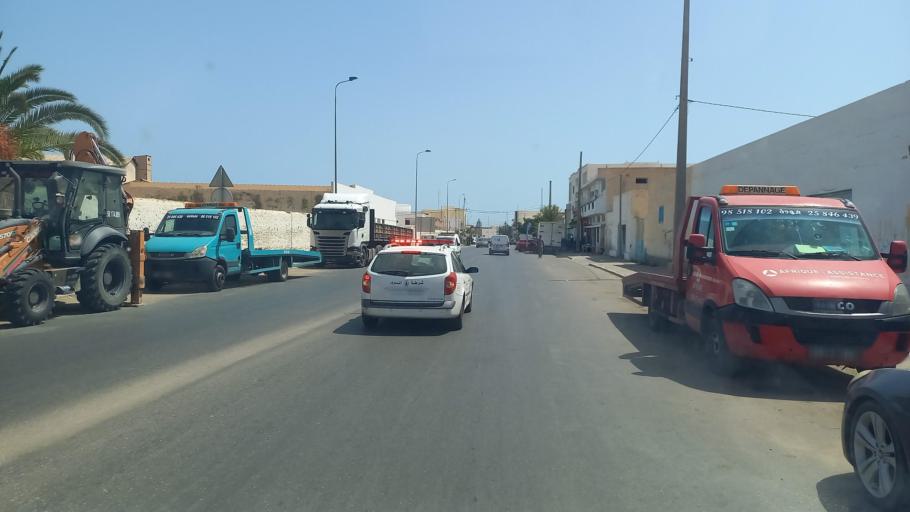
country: TN
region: Madanin
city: Zarzis
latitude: 33.4980
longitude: 11.0929
